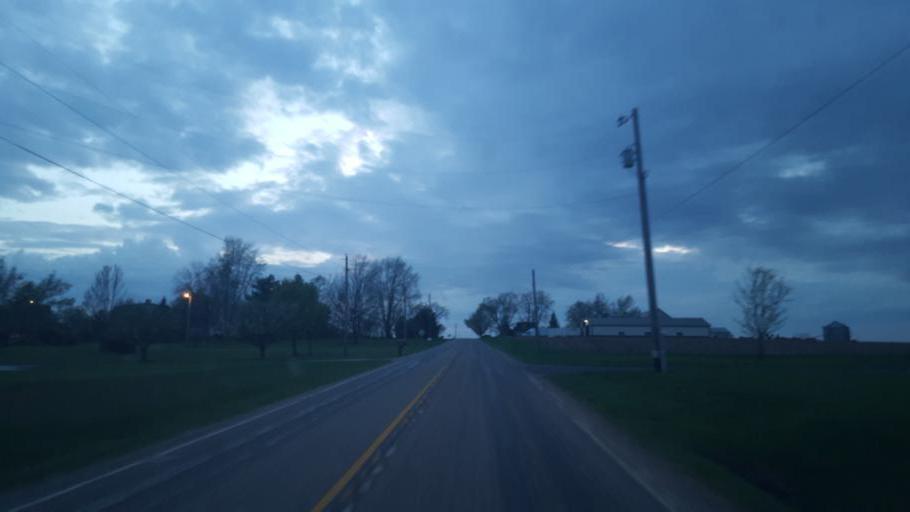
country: US
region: Ohio
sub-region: Ashland County
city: Ashland
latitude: 40.8660
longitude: -82.3885
